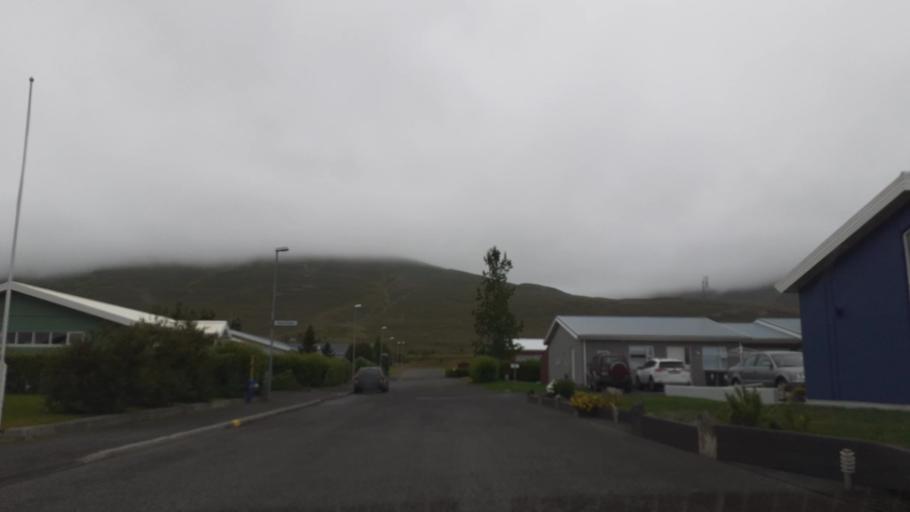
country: IS
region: Northeast
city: Dalvik
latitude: 65.9690
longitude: -18.5406
